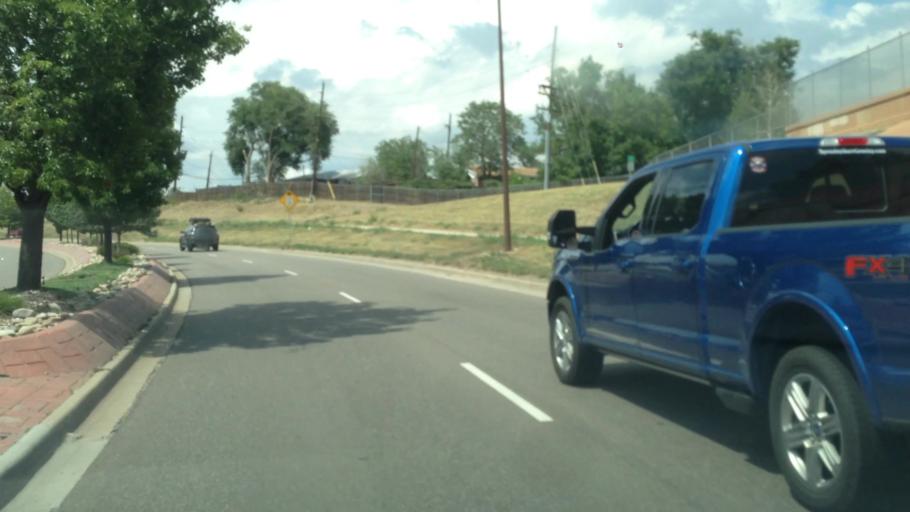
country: US
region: Colorado
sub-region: Jefferson County
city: Arvada
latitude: 39.7936
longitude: -105.1093
